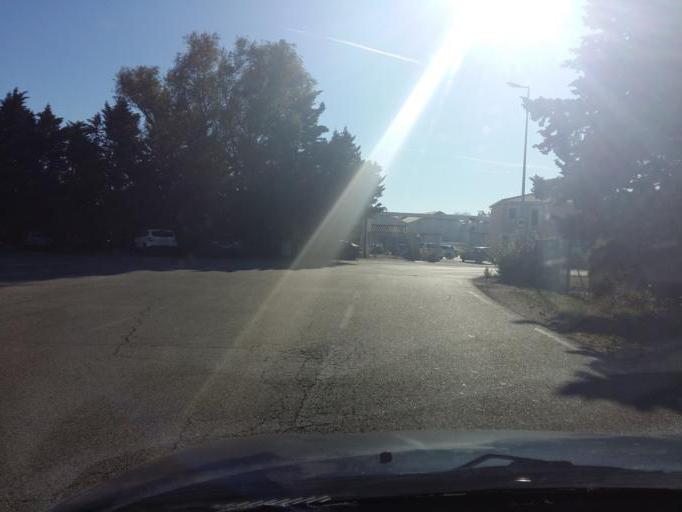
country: FR
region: Provence-Alpes-Cote d'Azur
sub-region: Departement du Vaucluse
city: Monteux
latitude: 44.0307
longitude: 4.9695
